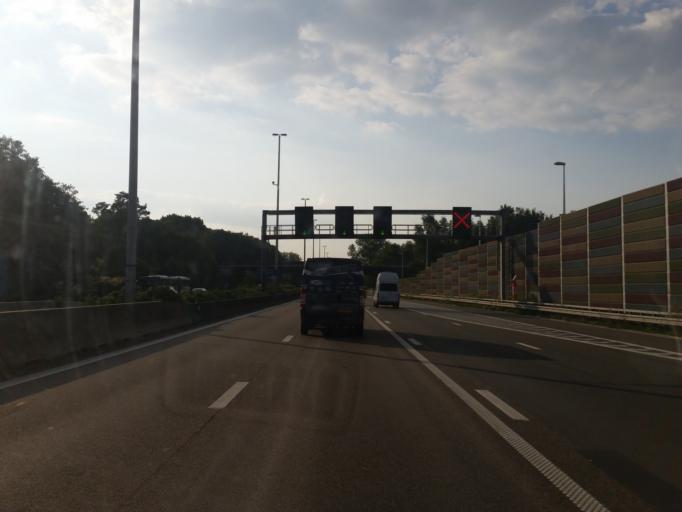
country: BE
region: Flanders
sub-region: Provincie Antwerpen
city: Ranst
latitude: 51.2025
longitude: 4.5729
